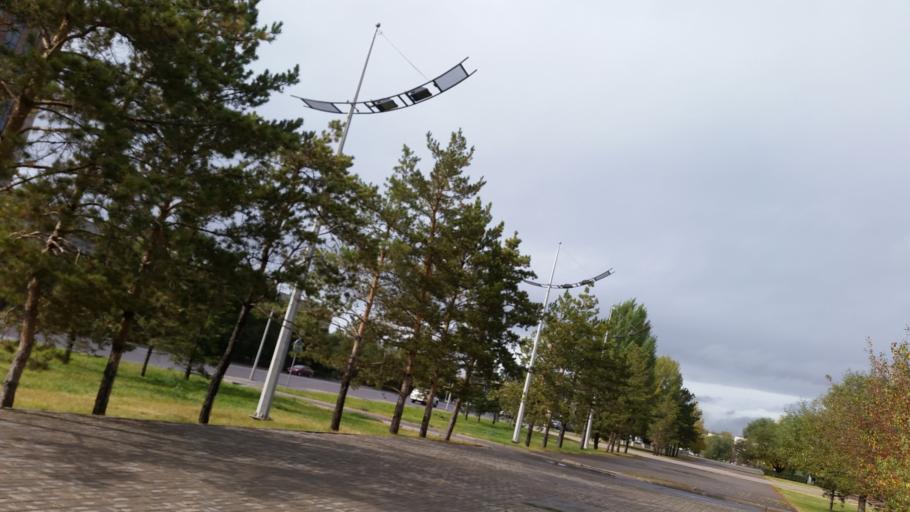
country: KZ
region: Astana Qalasy
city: Astana
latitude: 51.1525
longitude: 71.4562
